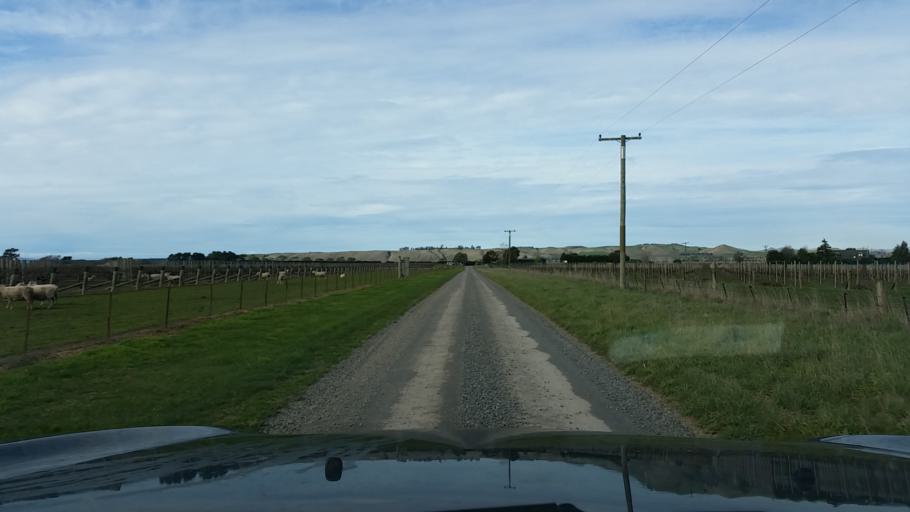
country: NZ
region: Marlborough
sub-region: Marlborough District
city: Blenheim
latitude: -41.6429
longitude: 174.0434
